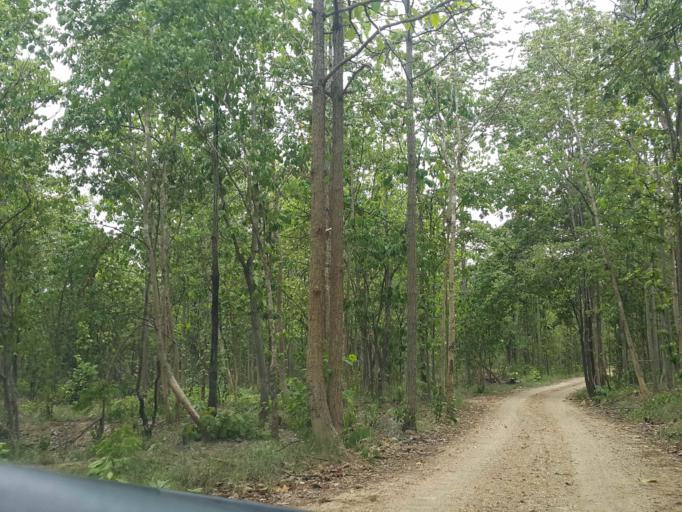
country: TH
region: Chiang Mai
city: Doi Lo
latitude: 18.5006
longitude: 98.7457
